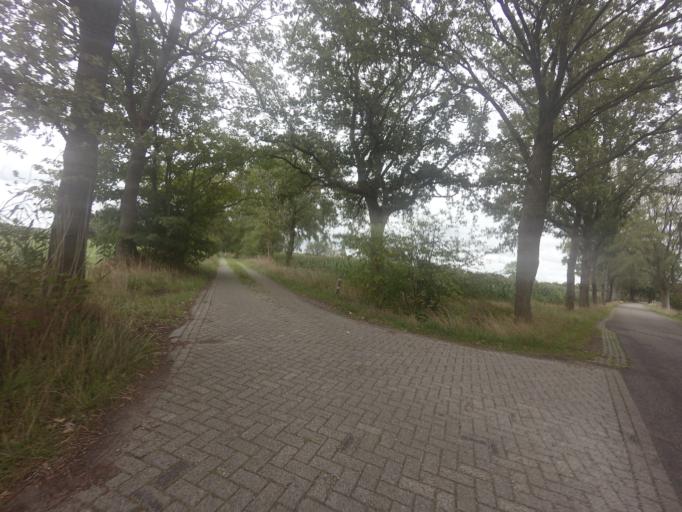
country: NL
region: Friesland
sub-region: Gemeente Weststellingwerf
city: Noordwolde
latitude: 52.9326
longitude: 6.1667
